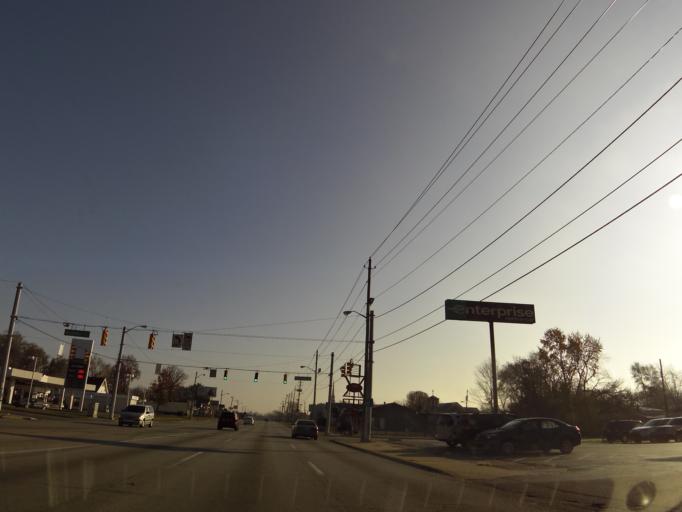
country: US
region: Indiana
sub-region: Marion County
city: Indianapolis
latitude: 39.7879
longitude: -86.2117
